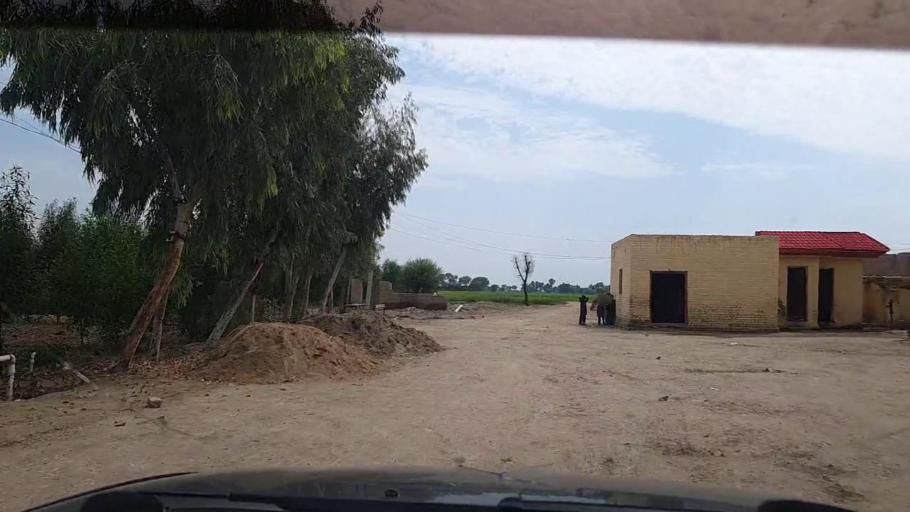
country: PK
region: Sindh
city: Thul
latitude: 28.2402
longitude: 68.7229
